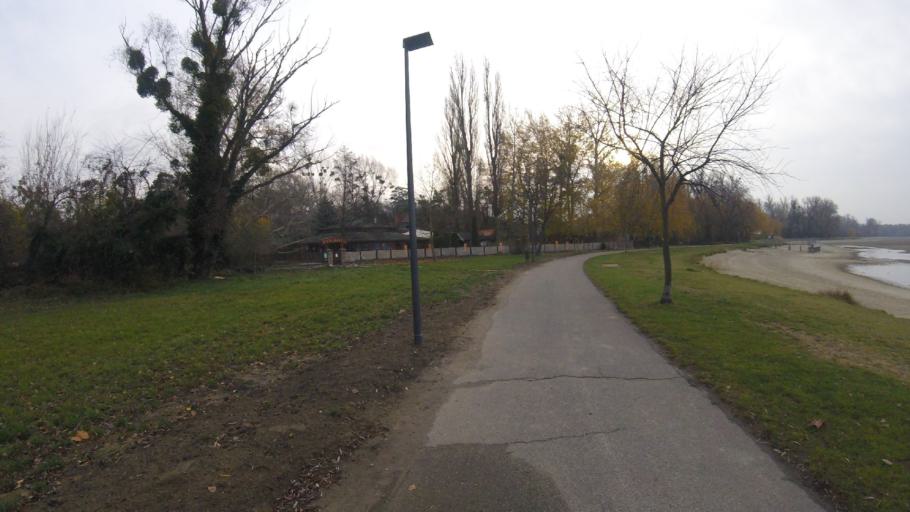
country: HU
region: Komarom-Esztergom
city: Tata
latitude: 47.6430
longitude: 18.3365
